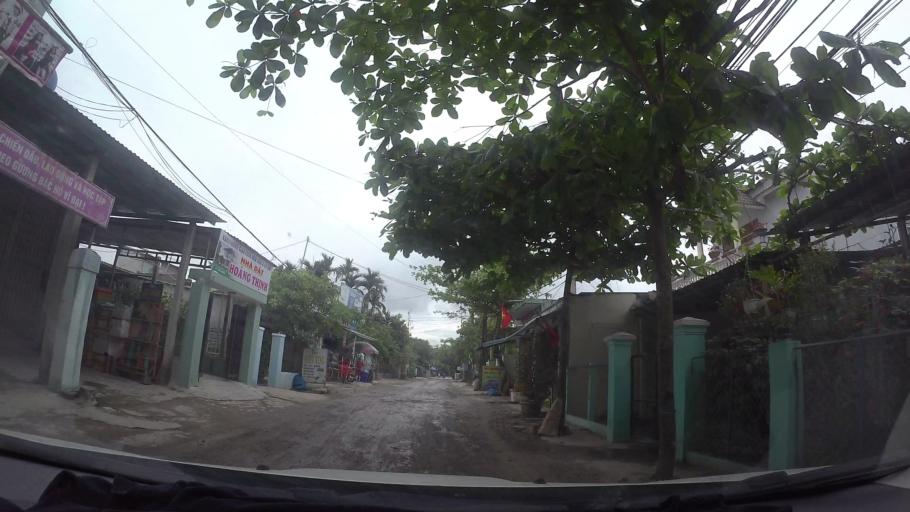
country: VN
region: Da Nang
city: Lien Chieu
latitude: 16.0775
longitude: 108.0989
